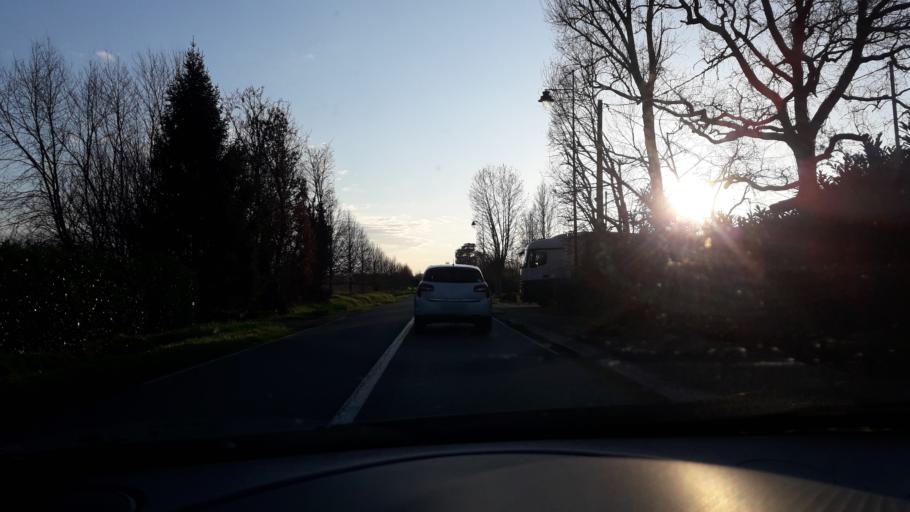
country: FR
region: Midi-Pyrenees
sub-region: Departement de la Haute-Garonne
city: Levignac
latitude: 43.6548
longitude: 1.1776
